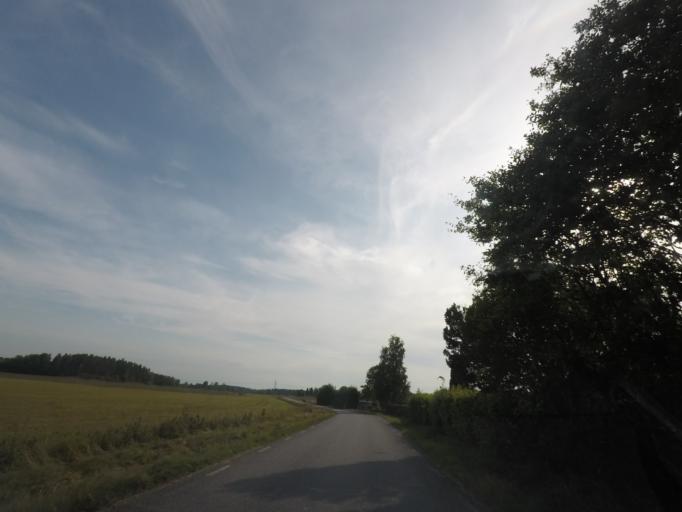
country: SE
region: Vaestmanland
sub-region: Hallstahammars Kommun
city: Kolback
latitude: 59.5331
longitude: 16.1411
